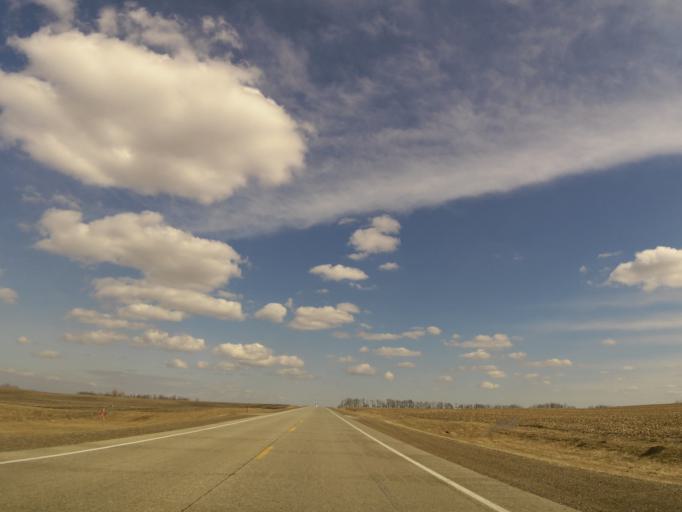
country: US
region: South Dakota
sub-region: Deuel County
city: Clear Lake
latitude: 44.8902
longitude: -96.8122
